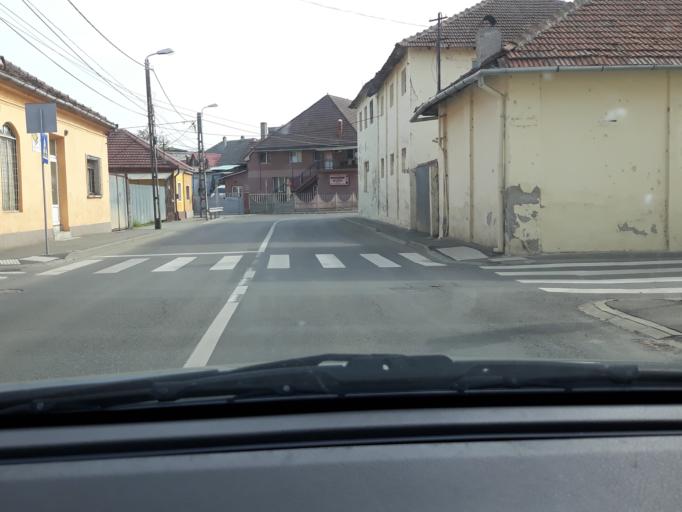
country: RO
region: Bihor
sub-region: Comuna Biharea
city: Oradea
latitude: 47.0386
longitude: 21.9557
